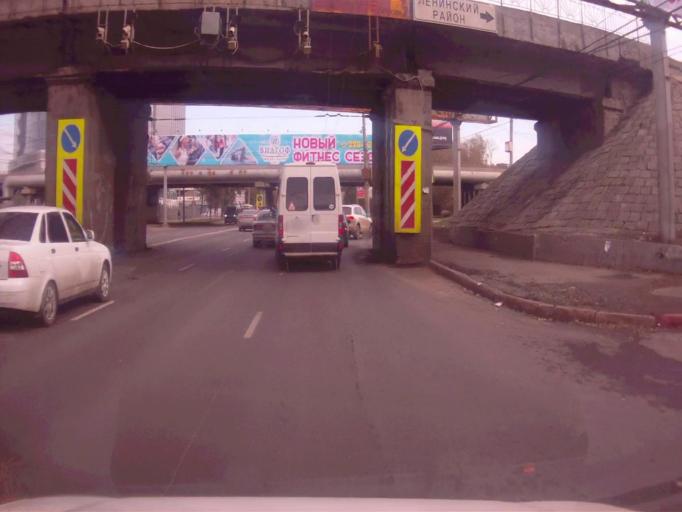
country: RU
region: Chelyabinsk
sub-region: Gorod Chelyabinsk
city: Chelyabinsk
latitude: 55.1610
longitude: 61.4272
